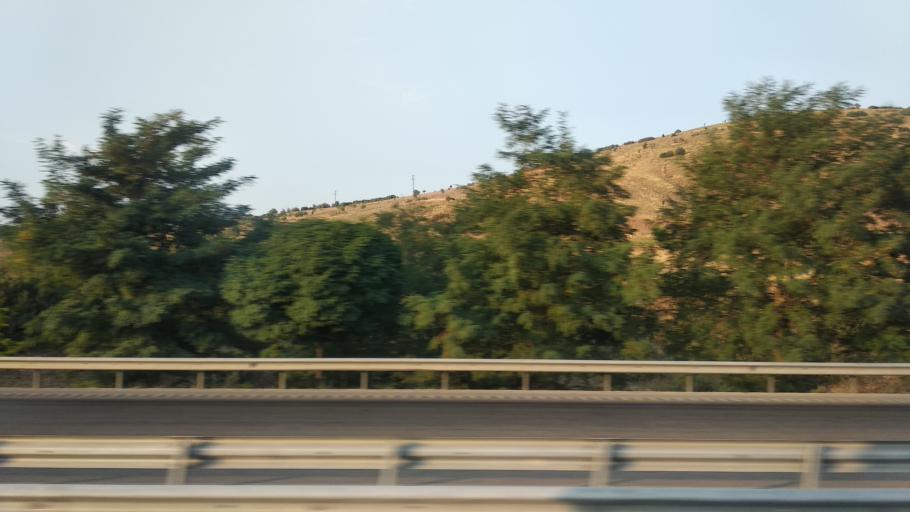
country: TR
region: Manisa
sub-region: Kula
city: Kula
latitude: 38.5661
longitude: 28.5841
